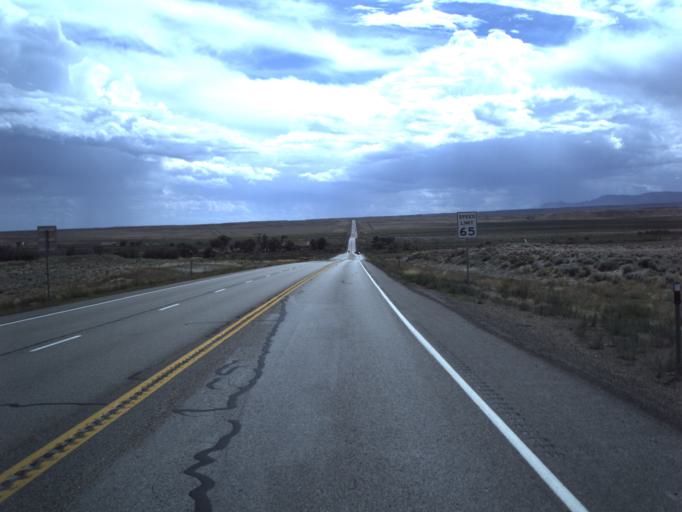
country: US
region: Utah
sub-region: Carbon County
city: Price
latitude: 39.5304
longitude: -110.8192
